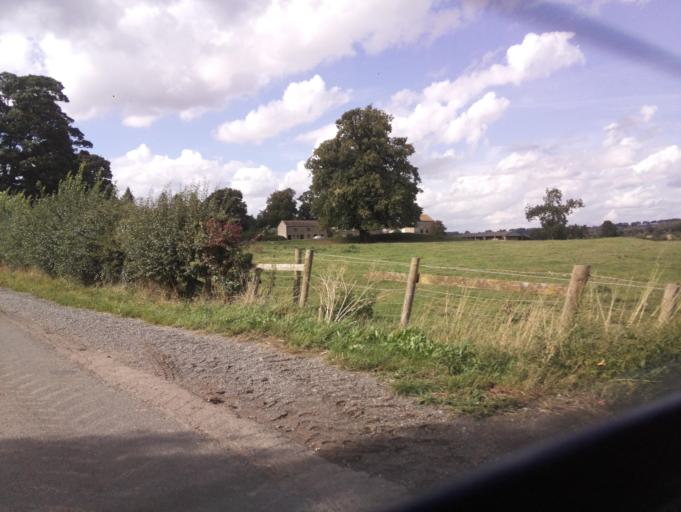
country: GB
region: England
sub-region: North Yorkshire
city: Leyburn
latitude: 54.2685
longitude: -1.7640
